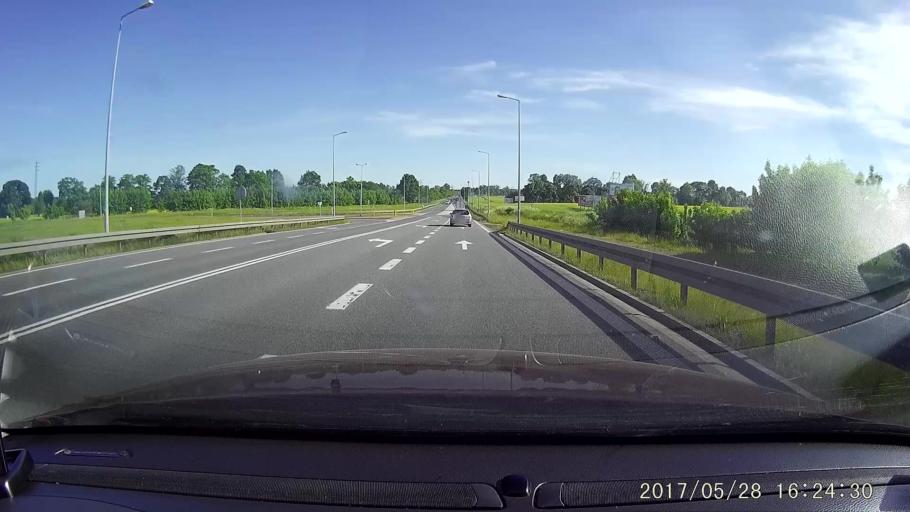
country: PL
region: Lower Silesian Voivodeship
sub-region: Powiat zgorzelecki
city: Lagow
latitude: 51.1709
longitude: 15.0299
